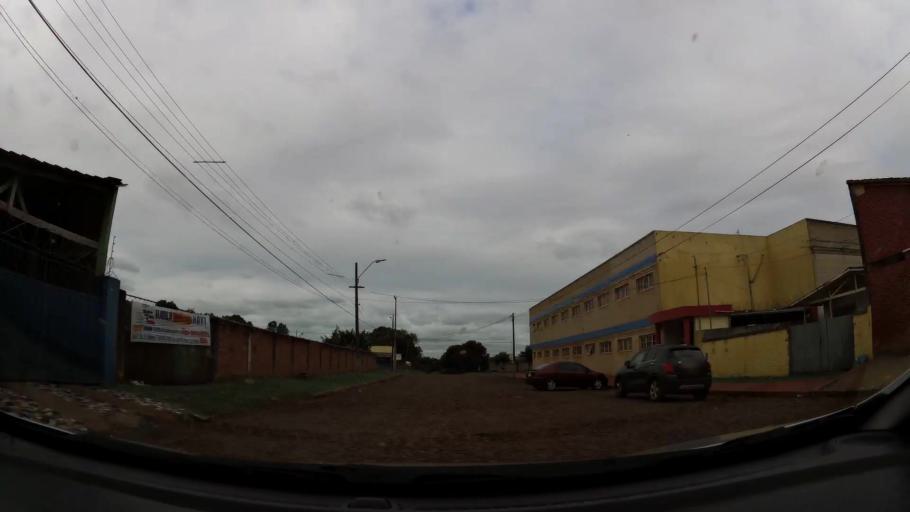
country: PY
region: Alto Parana
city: Ciudad del Este
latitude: -25.3989
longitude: -54.6401
